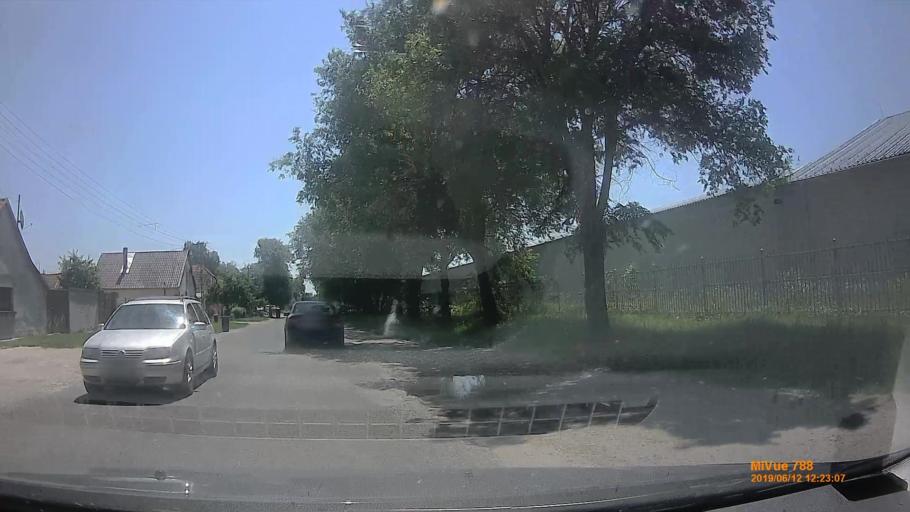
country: HU
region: Bacs-Kiskun
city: Kecskemet
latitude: 46.8941
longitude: 19.7000
